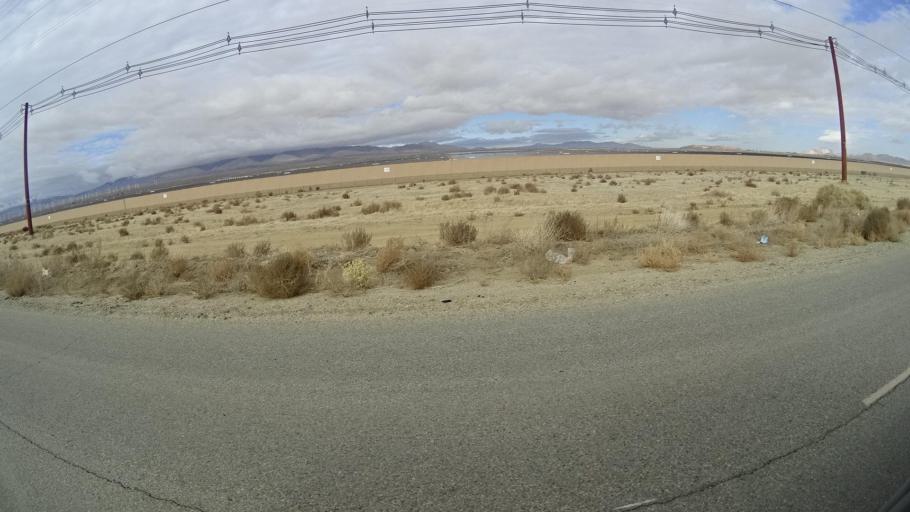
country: US
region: California
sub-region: Kern County
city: Rosamond
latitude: 34.8631
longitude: -118.3556
